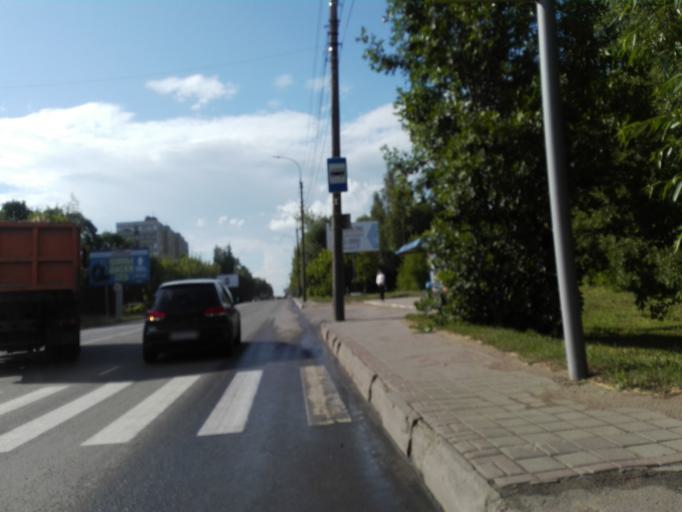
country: RU
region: Orjol
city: Orel
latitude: 52.9900
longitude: 36.1185
